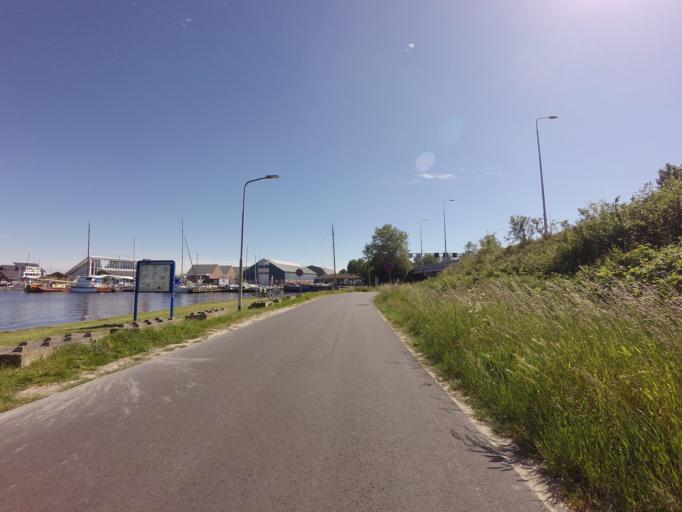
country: NL
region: North Holland
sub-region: Gemeente Uitgeest
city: Uitgeest
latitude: 52.5295
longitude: 4.7215
